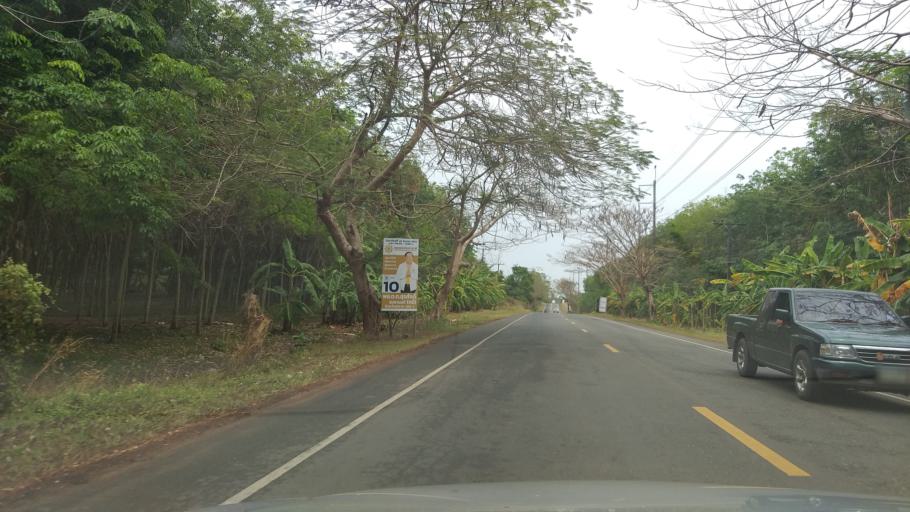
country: TH
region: Trat
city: Laem Ngop
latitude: 12.2616
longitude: 102.2949
